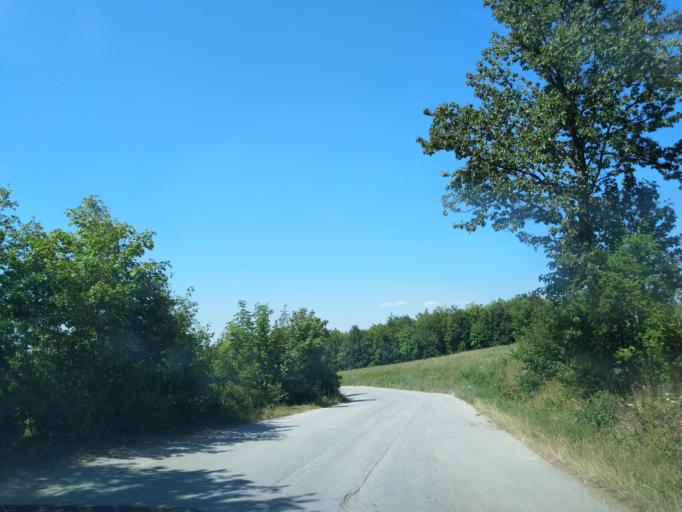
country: RS
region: Central Serbia
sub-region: Zlatiborski Okrug
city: Uzice
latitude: 43.8165
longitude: 19.8565
